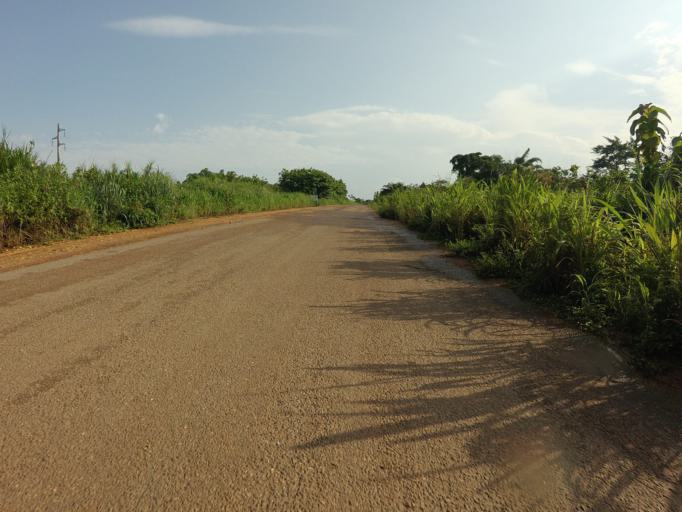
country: GH
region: Volta
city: Hohoe
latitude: 7.0834
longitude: 0.4438
